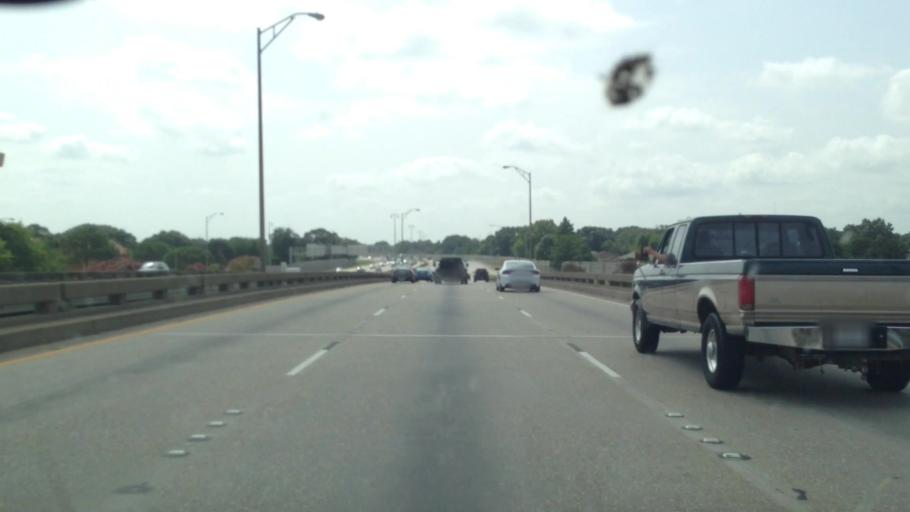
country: US
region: Louisiana
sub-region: Jefferson Parish
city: Kenner
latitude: 30.0050
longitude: -90.2084
